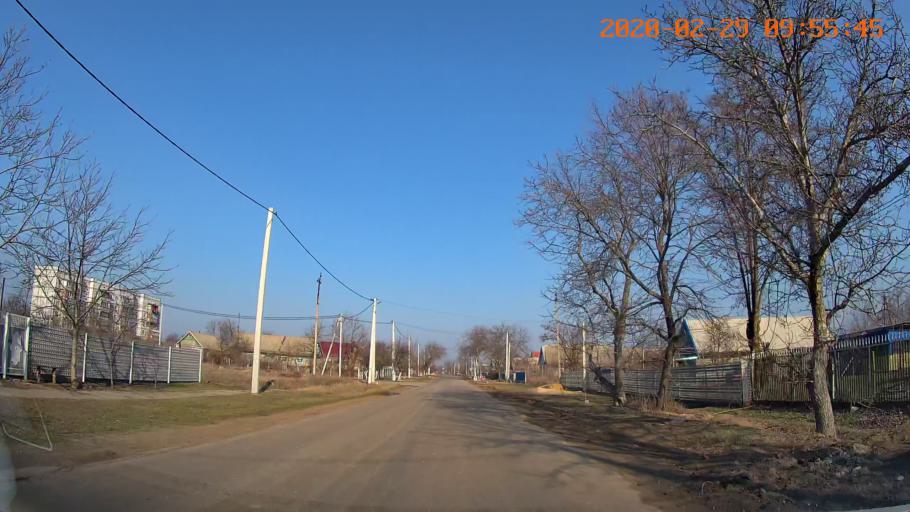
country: MD
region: Telenesti
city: Slobozia
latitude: 46.7366
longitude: 29.7085
